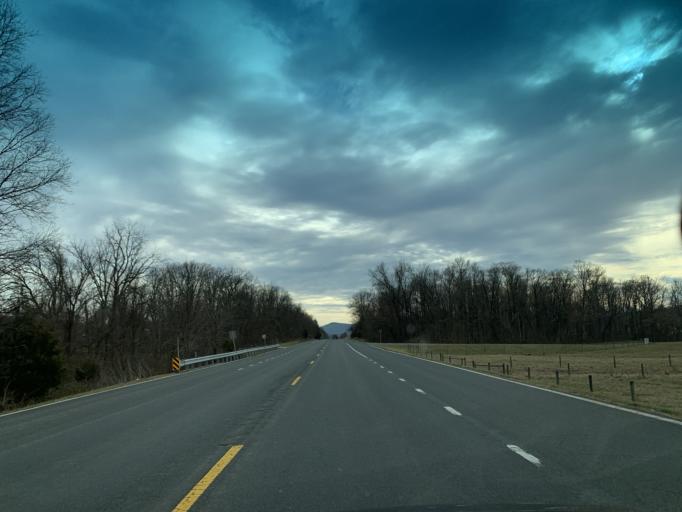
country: US
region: Maryland
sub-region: Washington County
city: Boonsboro
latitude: 39.4833
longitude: -77.6514
